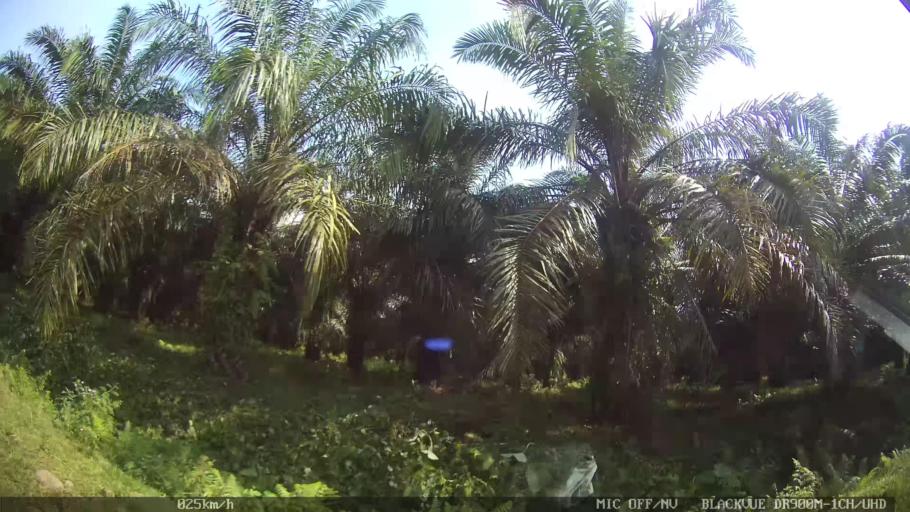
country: ID
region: North Sumatra
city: Binjai
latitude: 3.6425
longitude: 98.5321
